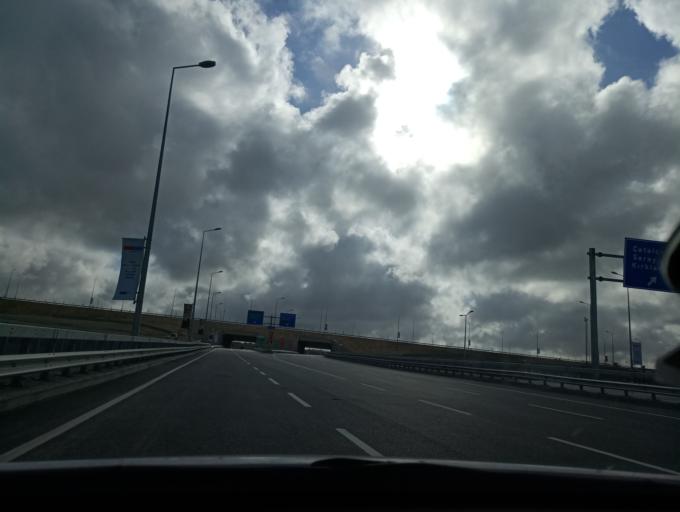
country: TR
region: Istanbul
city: Durusu
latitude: 41.2482
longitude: 28.7391
